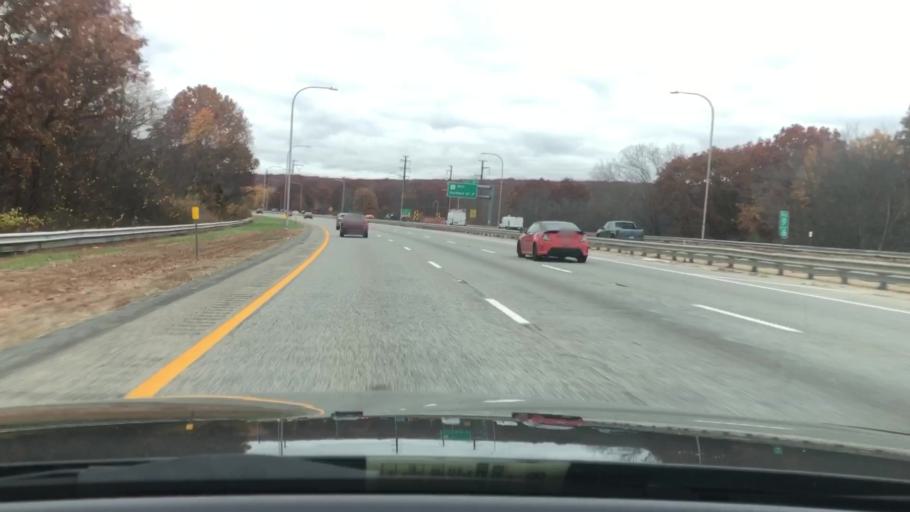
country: US
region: Rhode Island
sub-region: Providence County
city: Johnston
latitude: 41.8347
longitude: -71.5187
